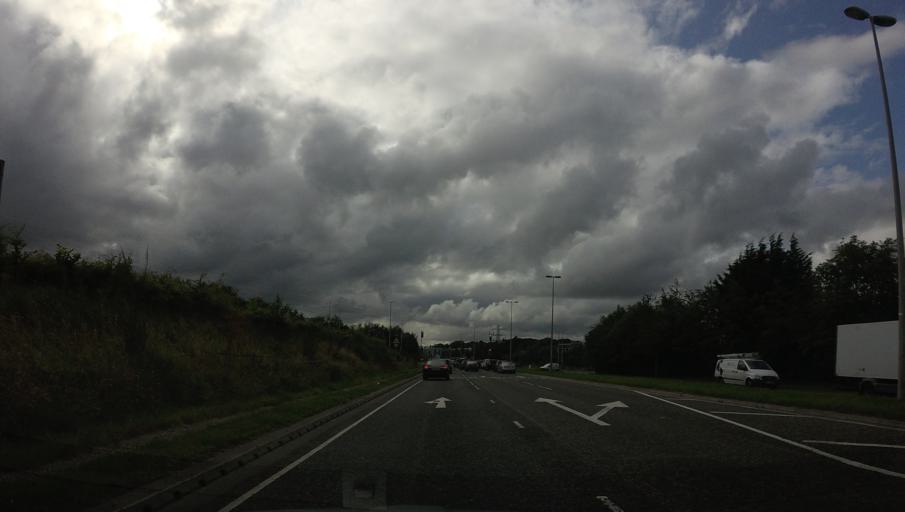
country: GB
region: Scotland
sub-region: Aberdeen City
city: Cults
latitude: 57.1464
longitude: -2.2178
